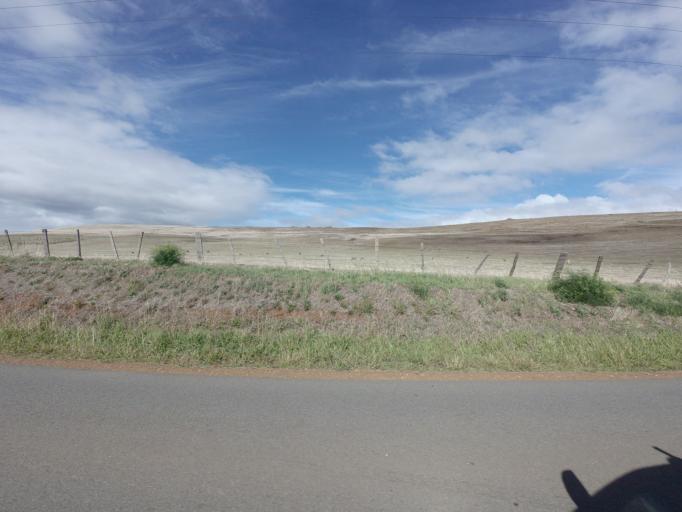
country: AU
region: Tasmania
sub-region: Derwent Valley
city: New Norfolk
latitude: -42.6962
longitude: 146.9318
